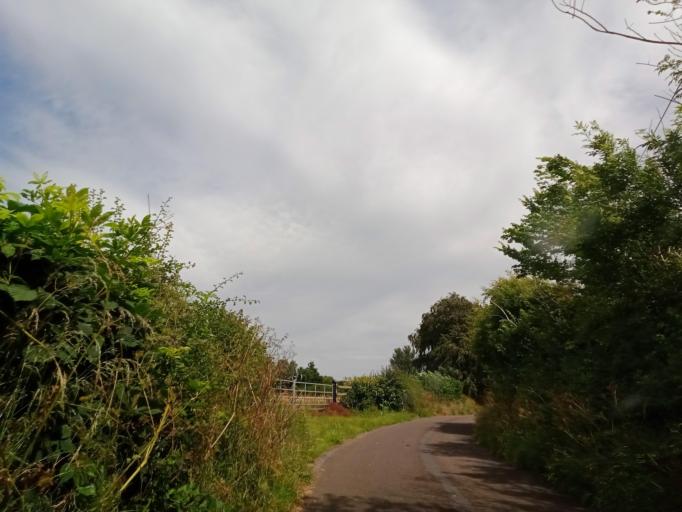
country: IE
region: Leinster
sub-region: Kilkenny
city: Thomastown
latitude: 52.5855
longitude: -7.1210
